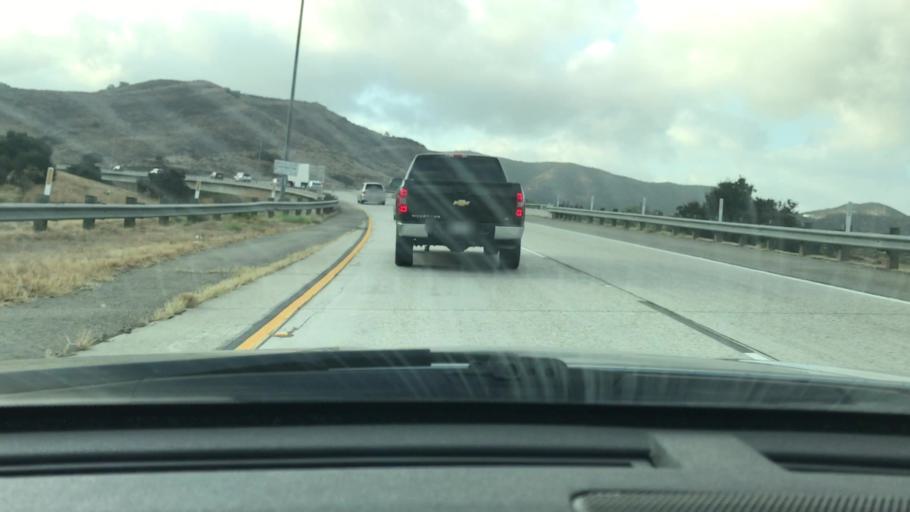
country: US
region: California
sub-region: Ventura County
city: Thousand Oaks
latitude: 34.1778
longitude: -118.8608
